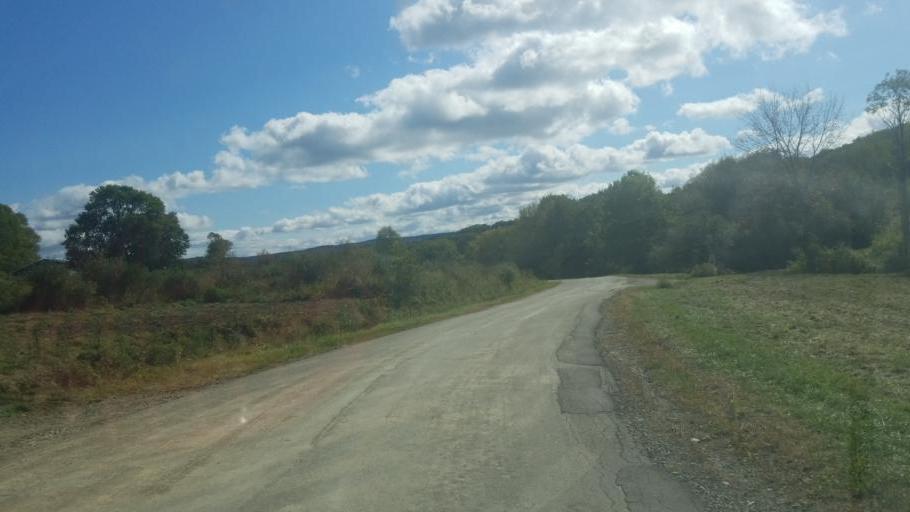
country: US
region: New York
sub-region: Allegany County
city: Cuba
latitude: 42.1705
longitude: -78.3458
